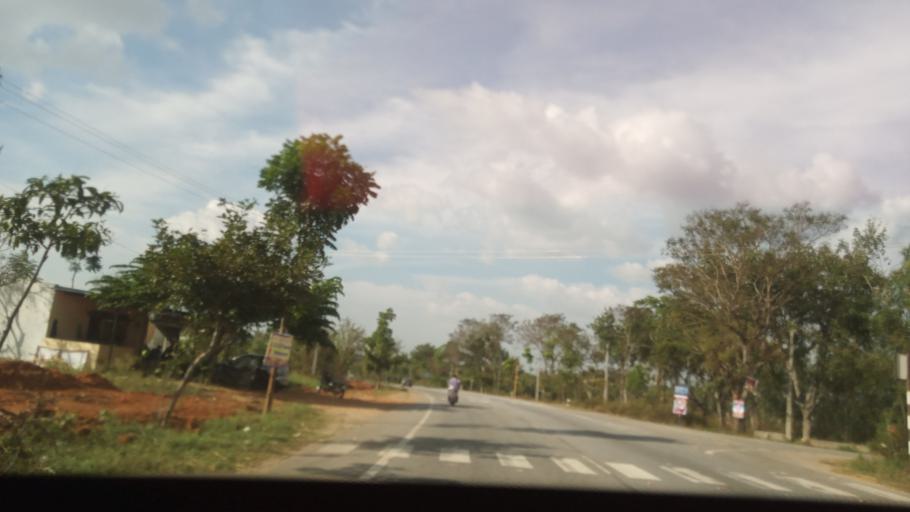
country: IN
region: Karnataka
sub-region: Mandya
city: Maddur
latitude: 12.6382
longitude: 77.0565
